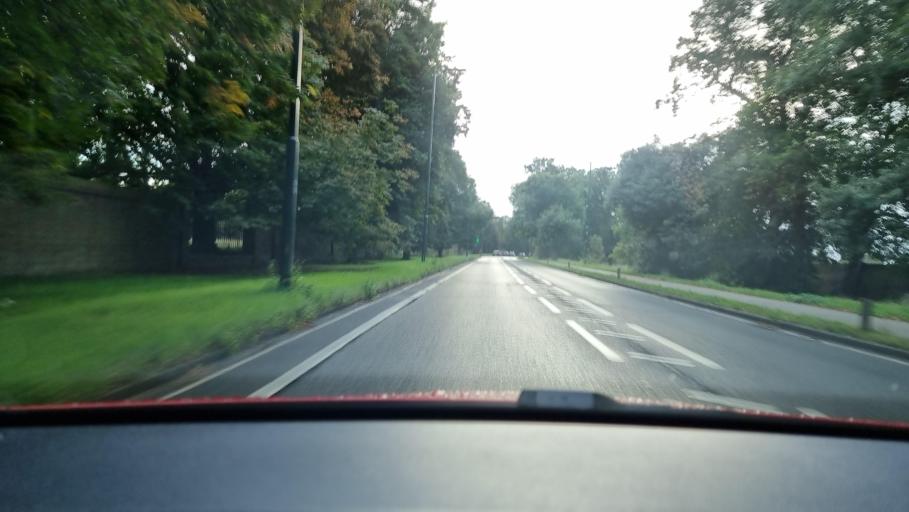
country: GB
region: England
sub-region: Greater London
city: Teddington
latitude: 51.4087
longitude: -0.3192
